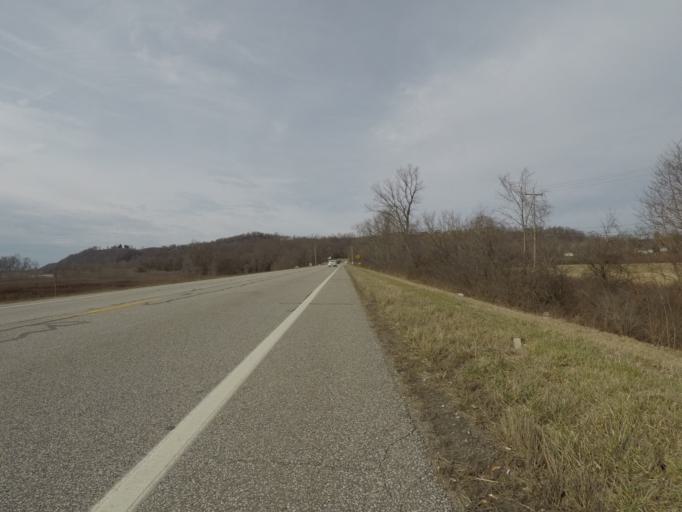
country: US
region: West Virginia
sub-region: Cabell County
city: Huntington
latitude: 38.4414
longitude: -82.3951
